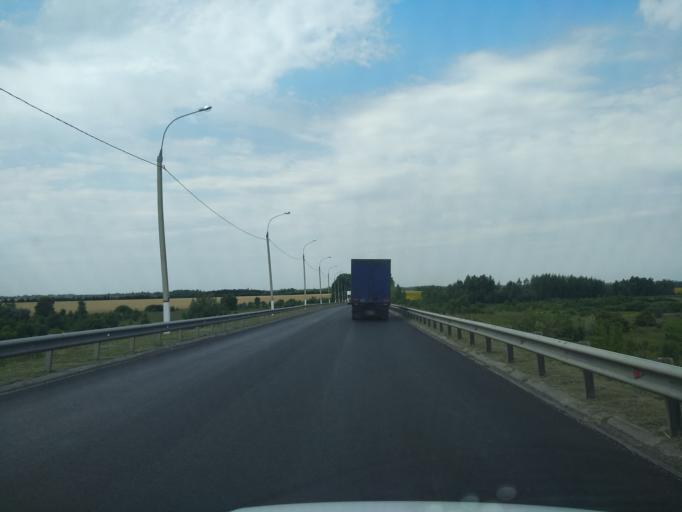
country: RU
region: Voronezj
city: Pereleshino
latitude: 51.7606
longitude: 40.1243
